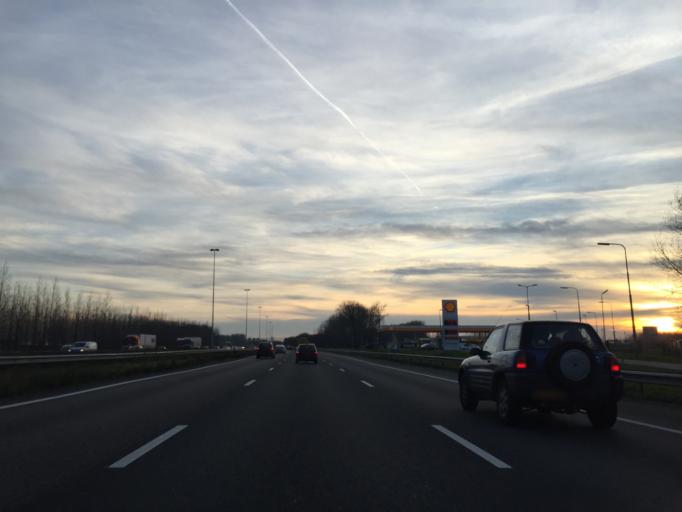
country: NL
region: South Holland
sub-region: Gemeente Zwijndrecht
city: Zwijndrecht
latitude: 51.7364
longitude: 4.6340
